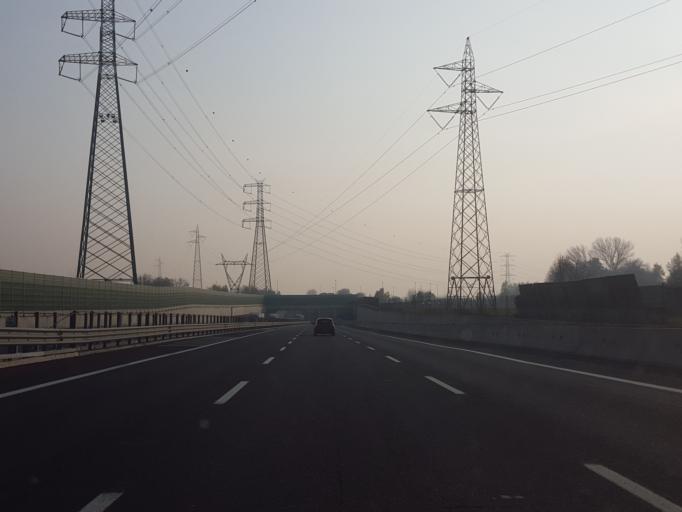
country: IT
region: Veneto
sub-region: Provincia di Venezia
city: Spinea-Orgnano
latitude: 45.4998
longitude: 12.1387
